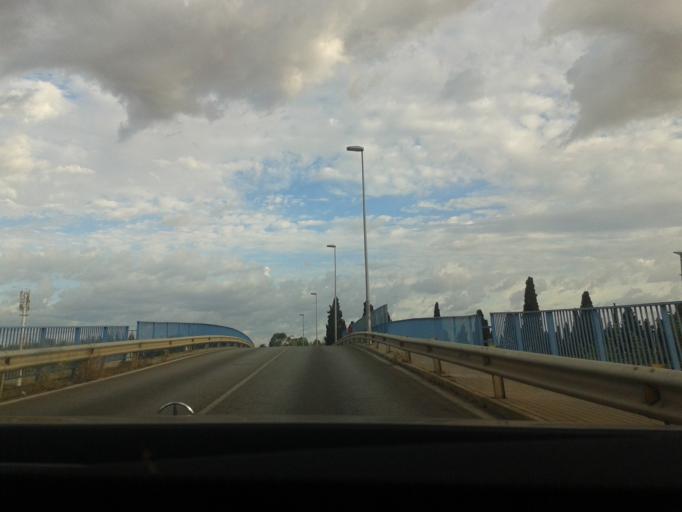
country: ES
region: Madrid
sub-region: Provincia de Madrid
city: Alcala de Henares
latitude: 40.4849
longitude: -3.3775
